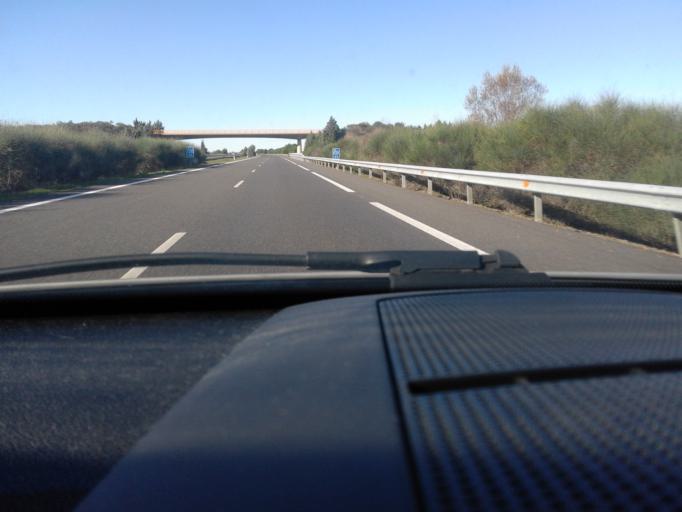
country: ES
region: Castille and Leon
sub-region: Provincia de Leon
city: Calzada del Coto
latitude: 42.3861
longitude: -5.0938
